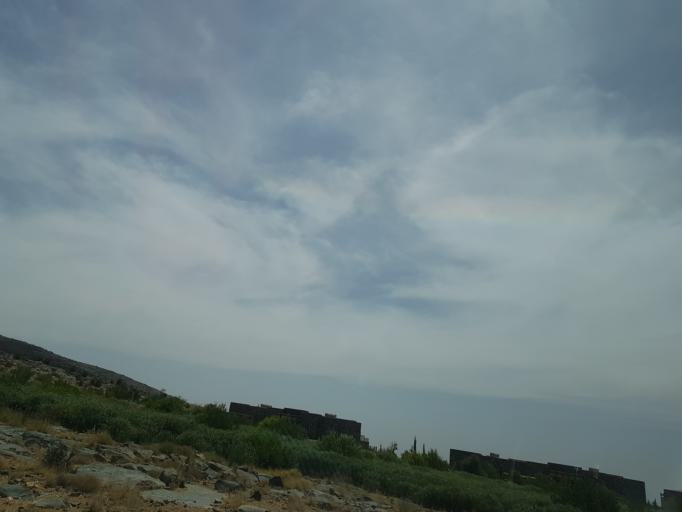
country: OM
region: Al Batinah
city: Bayt al `Awabi
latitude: 23.1427
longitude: 57.5347
